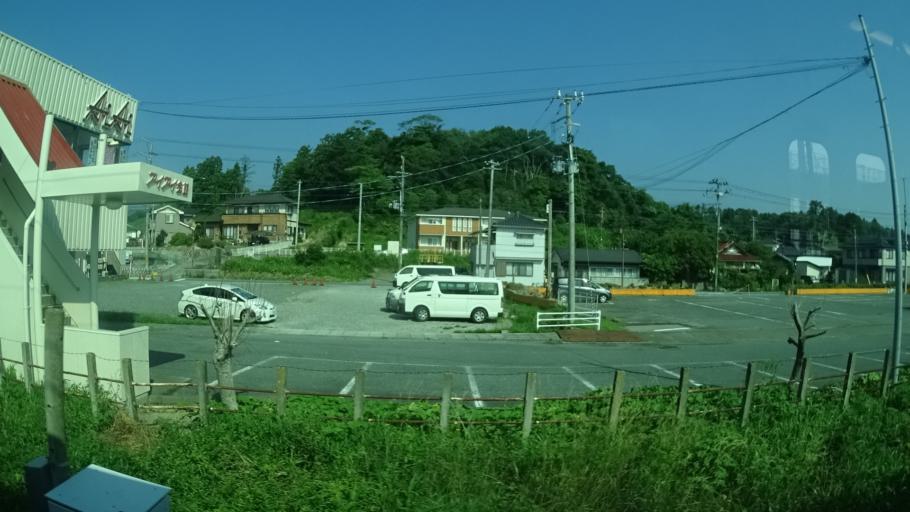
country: JP
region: Fukushima
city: Iwaki
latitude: 37.2137
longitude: 141.0004
